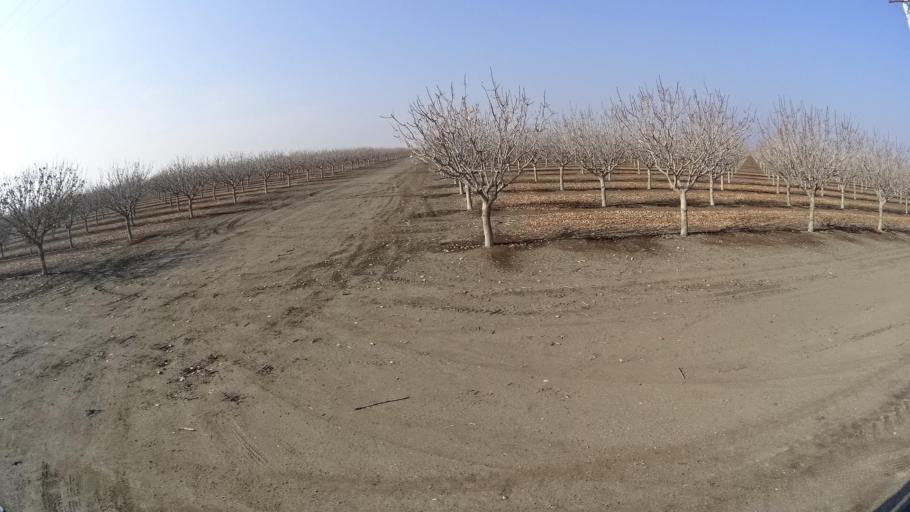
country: US
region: California
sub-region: Kern County
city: Buttonwillow
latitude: 35.3875
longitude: -119.4477
